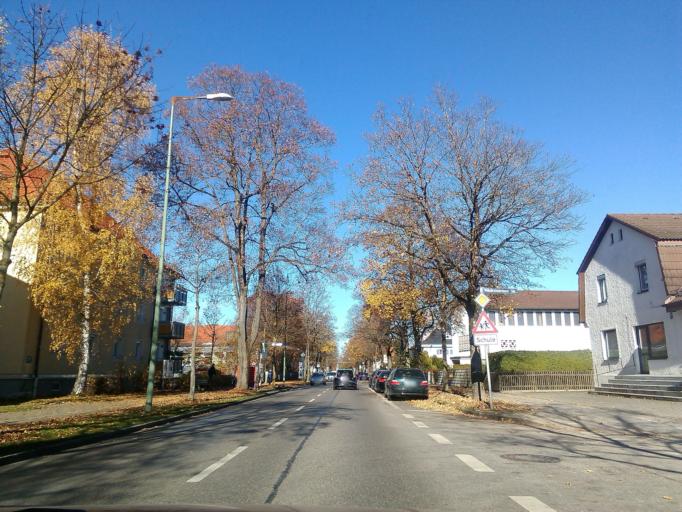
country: DE
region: Bavaria
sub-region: Upper Bavaria
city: Grafelfing
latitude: 48.1493
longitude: 11.4207
